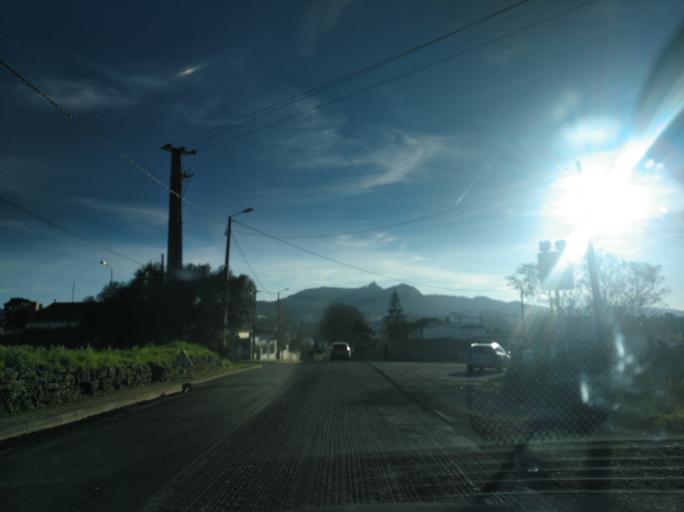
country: PT
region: Lisbon
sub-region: Sintra
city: Sintra
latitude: 38.8158
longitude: -9.3679
